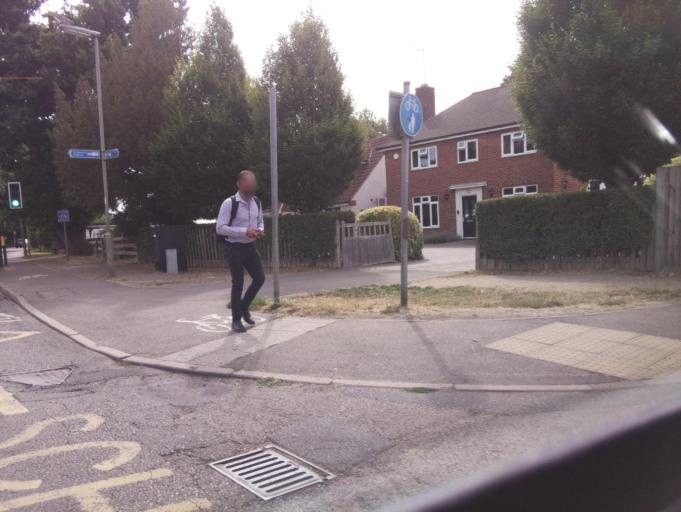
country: GB
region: England
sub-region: Surrey
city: Horley
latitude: 51.1749
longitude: -0.1559
